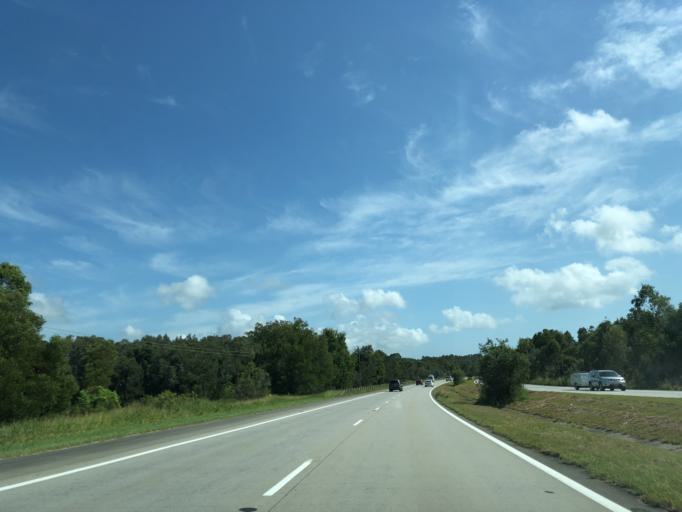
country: AU
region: New South Wales
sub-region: Byron Shire
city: Brunswick Heads
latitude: -28.5703
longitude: 153.5406
